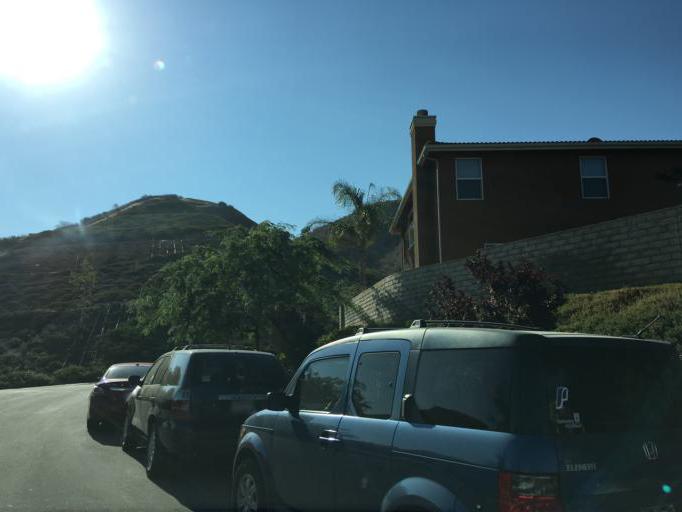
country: US
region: California
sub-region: Los Angeles County
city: Santa Clarita
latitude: 34.3725
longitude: -118.5916
